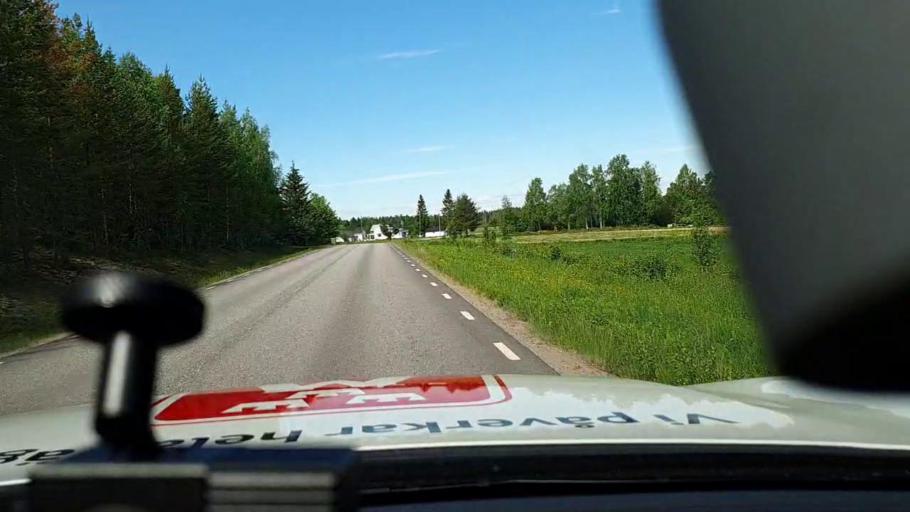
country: SE
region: Norrbotten
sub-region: Lulea Kommun
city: Sodra Sunderbyn
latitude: 65.6600
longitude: 21.8329
